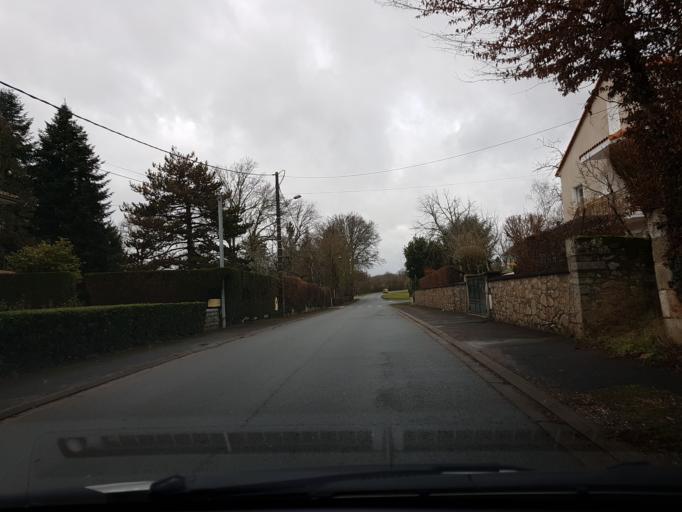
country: FR
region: Poitou-Charentes
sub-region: Departement de la Charente
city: Chabanais
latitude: 45.8801
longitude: 0.7213
